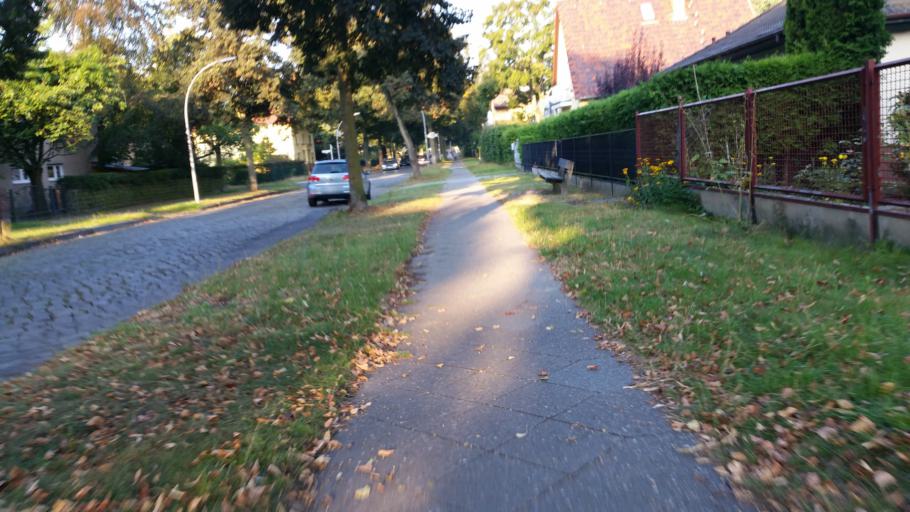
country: DE
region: Berlin
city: Lichtenrade
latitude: 52.4035
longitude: 13.3996
